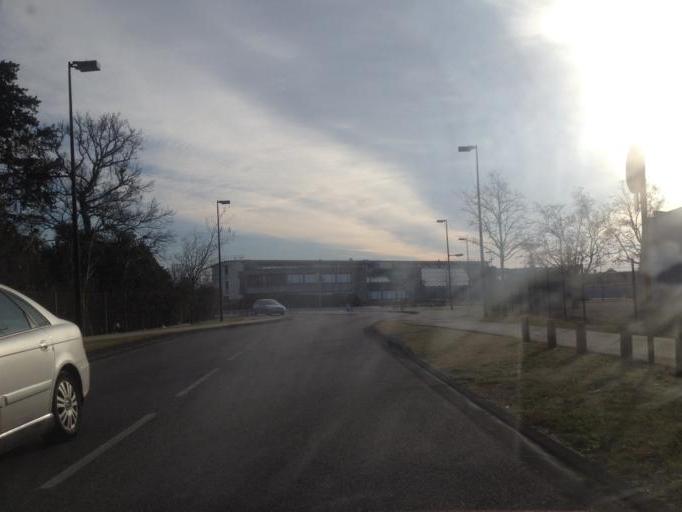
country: FR
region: Provence-Alpes-Cote d'Azur
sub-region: Departement du Vaucluse
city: Orange
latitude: 44.1293
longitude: 4.7978
